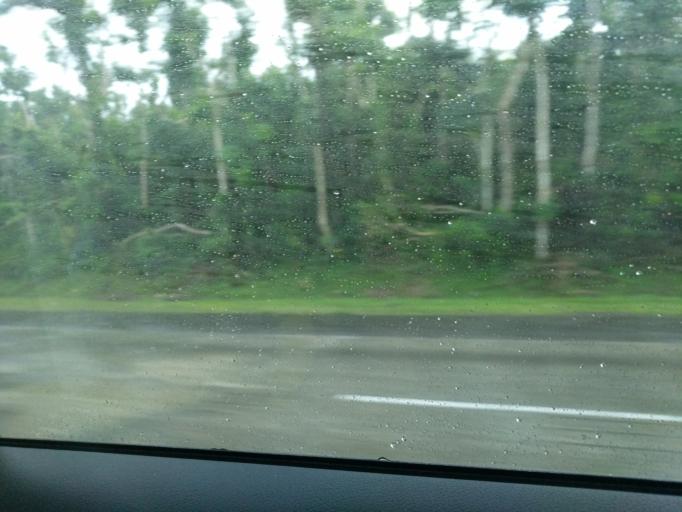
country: PR
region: Cidra
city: Bayamon
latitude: 18.1716
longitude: -66.0746
